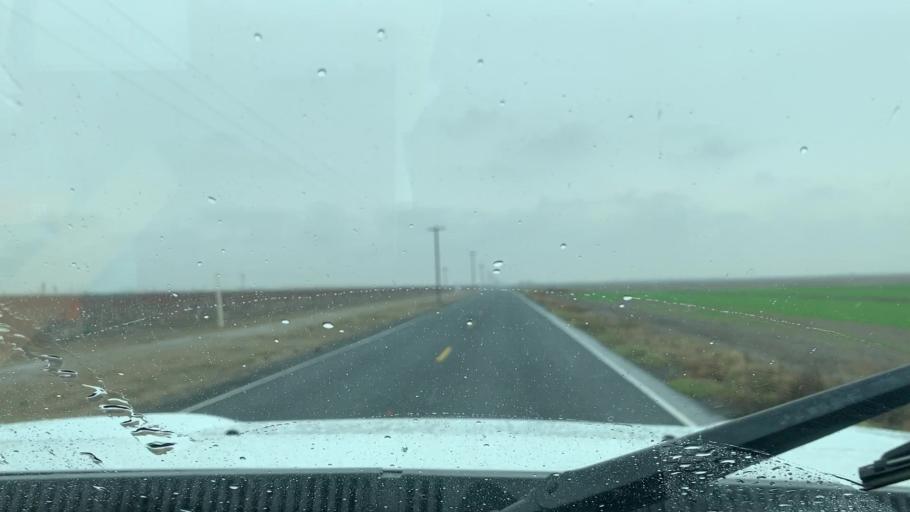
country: US
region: California
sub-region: Tulare County
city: Earlimart
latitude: 35.8917
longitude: -119.3785
